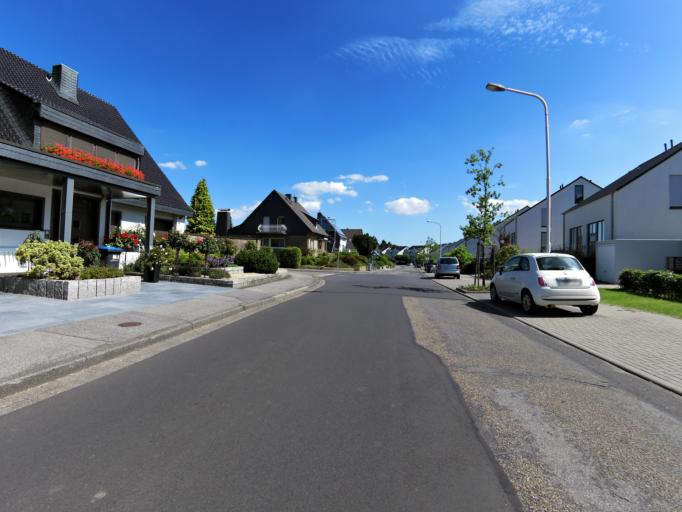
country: NL
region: Limburg
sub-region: Gemeente Kerkrade
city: Kerkrade
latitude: 50.8248
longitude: 6.0678
